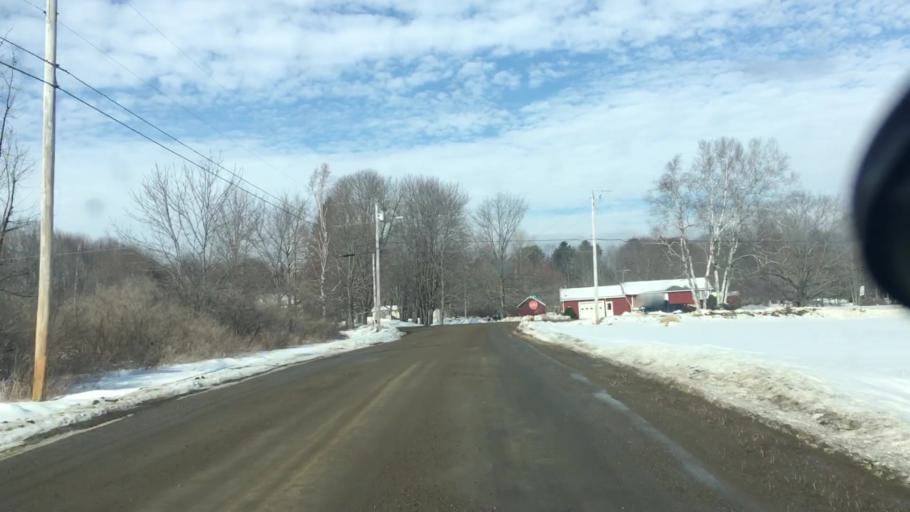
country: US
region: Maine
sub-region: Penobscot County
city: Levant
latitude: 44.8615
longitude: -68.8795
